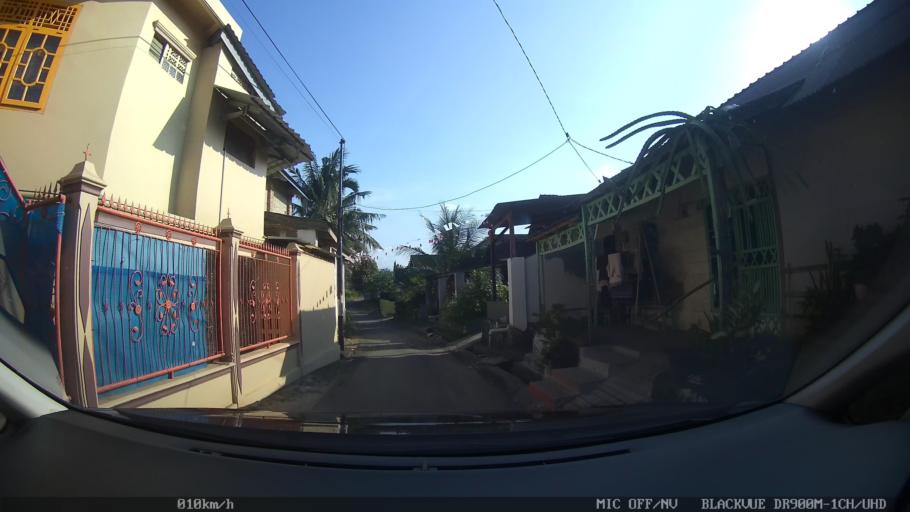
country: ID
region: Lampung
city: Kedaton
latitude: -5.3717
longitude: 105.2308
